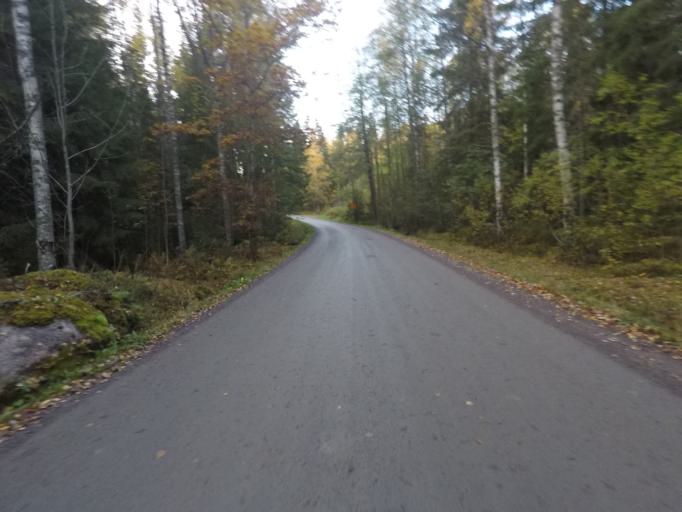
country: SE
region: OErebro
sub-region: Karlskoga Kommun
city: Karlskoga
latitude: 59.3005
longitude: 14.5071
